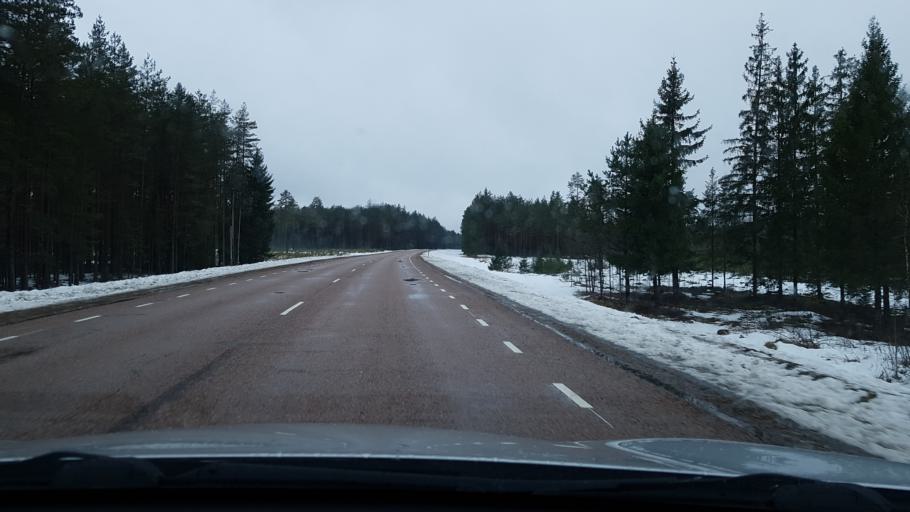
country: EE
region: Vorumaa
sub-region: Voru linn
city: Voru
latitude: 57.7636
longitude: 26.8494
